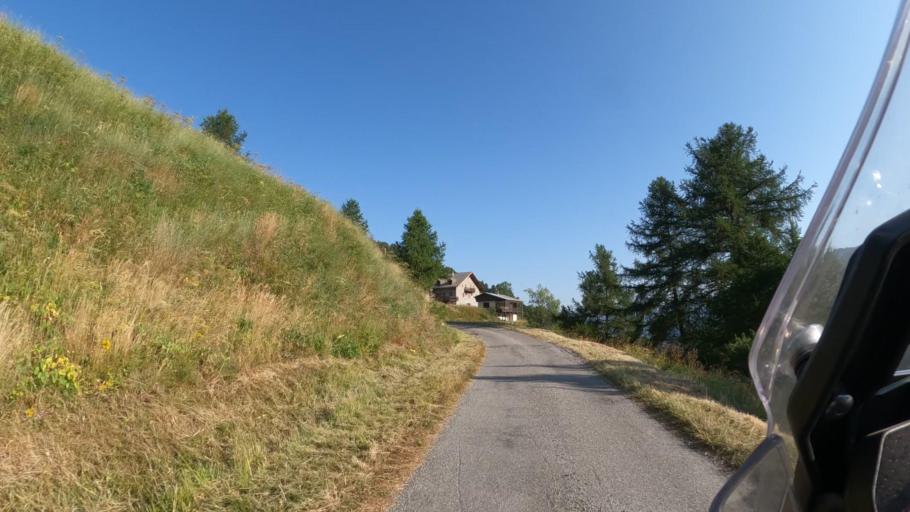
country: FR
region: Provence-Alpes-Cote d'Azur
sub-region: Departement des Hautes-Alpes
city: Guillestre
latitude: 44.5993
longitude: 6.6822
